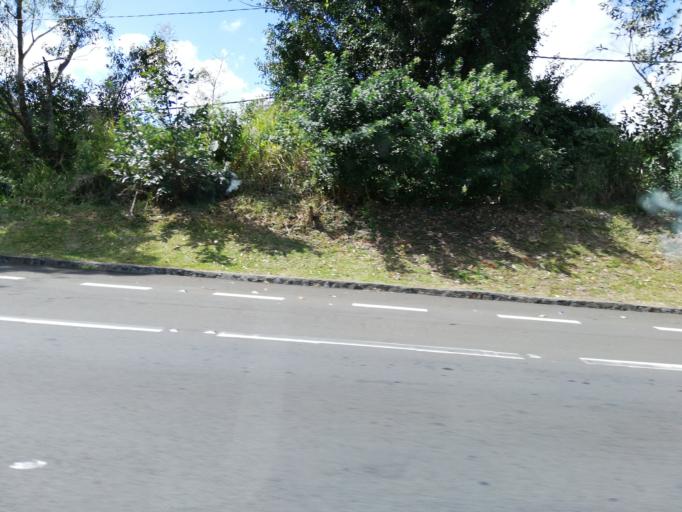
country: MU
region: Plaines Wilhems
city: Ebene
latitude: -20.2374
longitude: 57.4988
